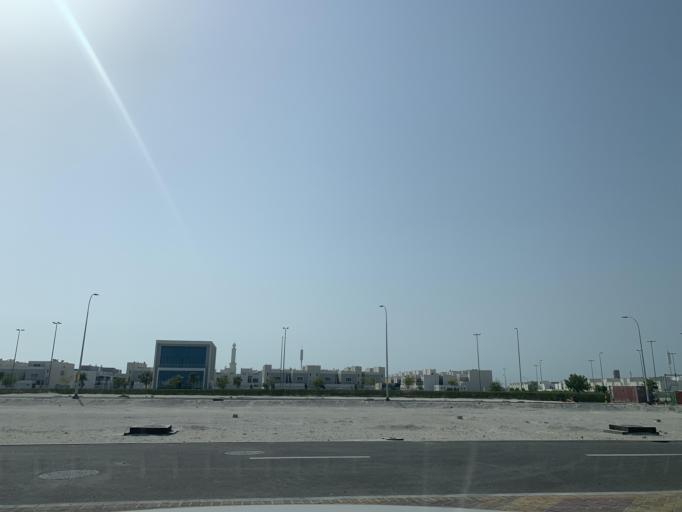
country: BH
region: Muharraq
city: Al Muharraq
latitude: 26.3081
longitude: 50.6314
